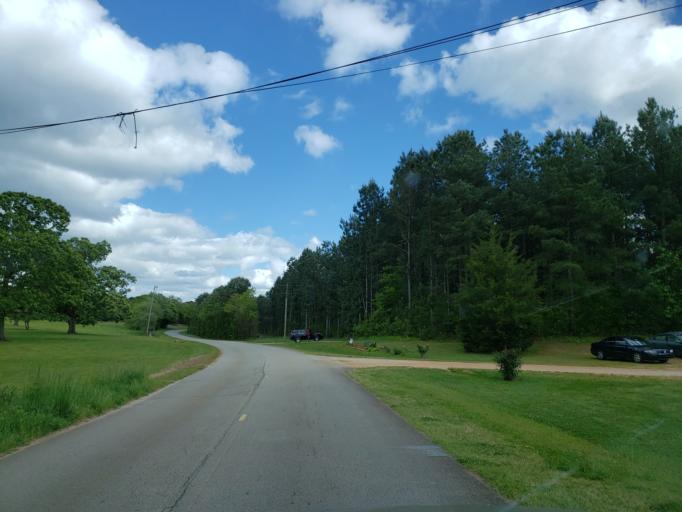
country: US
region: Georgia
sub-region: Haralson County
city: Tallapoosa
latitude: 33.6482
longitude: -85.2832
